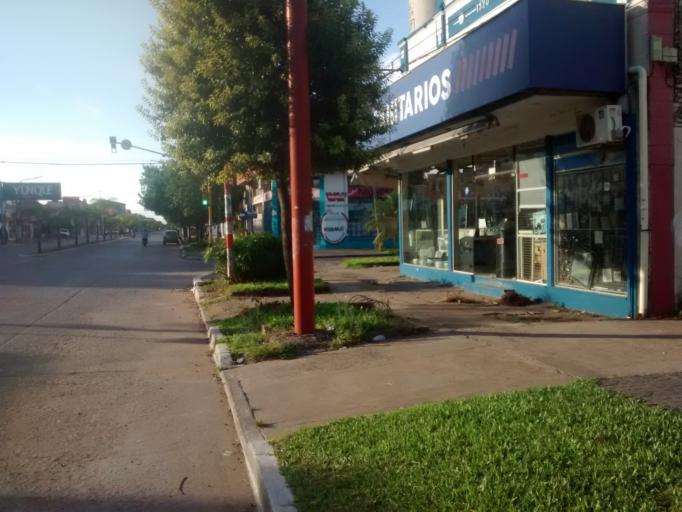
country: AR
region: Chaco
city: Resistencia
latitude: -27.4425
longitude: -58.9961
